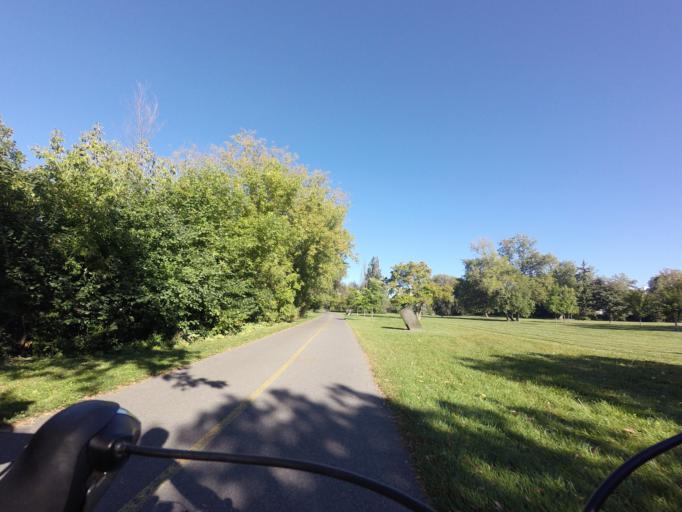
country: CA
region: Ontario
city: Ottawa
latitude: 45.4250
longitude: -75.6678
